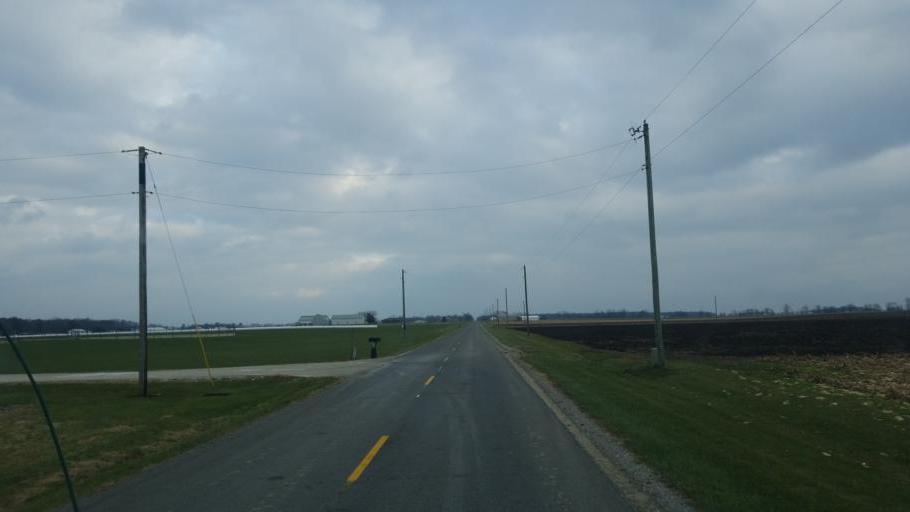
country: US
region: Ohio
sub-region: Mercer County
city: Coldwater
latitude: 40.5090
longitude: -84.6768
